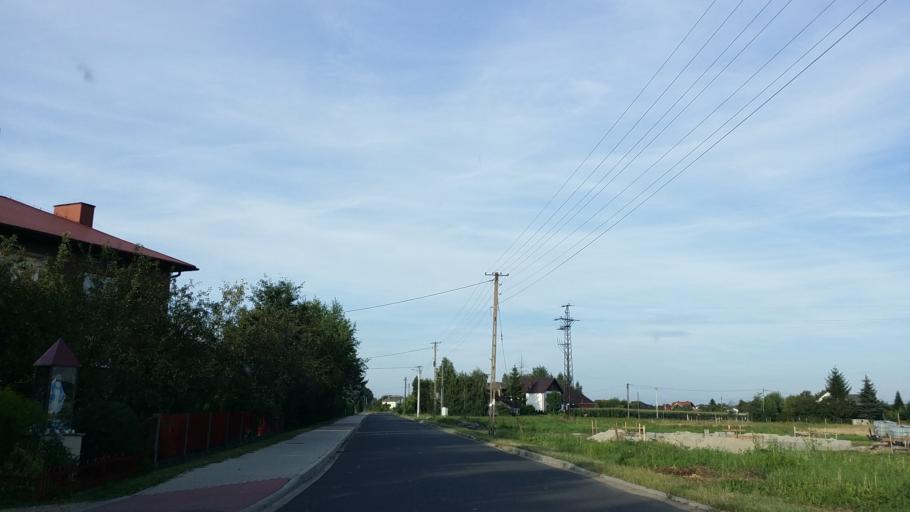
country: PL
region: Lesser Poland Voivodeship
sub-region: Powiat oswiecimski
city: Zator
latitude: 49.9853
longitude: 19.4074
